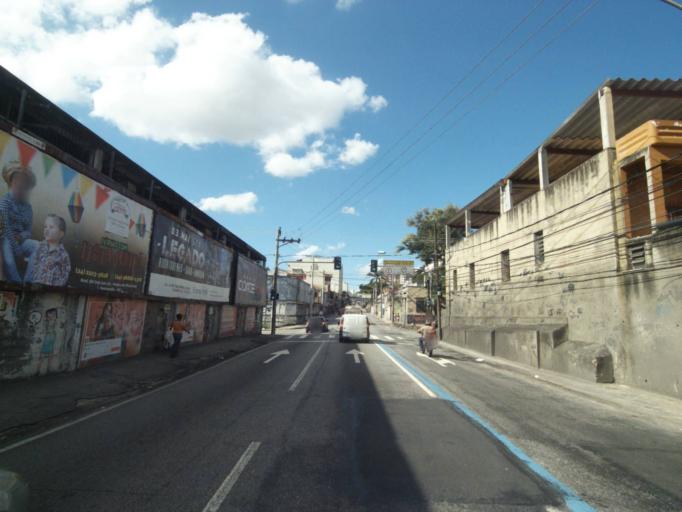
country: BR
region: Rio de Janeiro
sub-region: Rio De Janeiro
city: Rio de Janeiro
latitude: -22.9032
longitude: -43.2529
